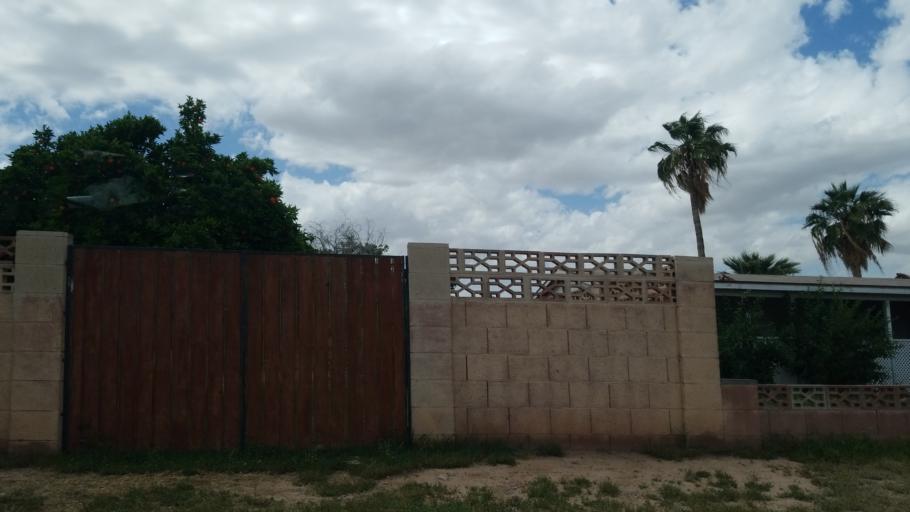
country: US
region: Arizona
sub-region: Maricopa County
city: Peoria
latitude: 33.6778
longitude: -112.1384
